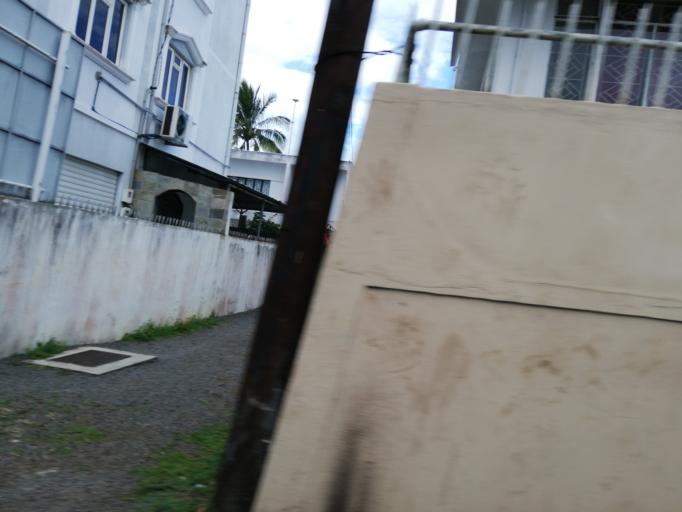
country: MU
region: Moka
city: Moka
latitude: -20.2245
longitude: 57.4637
